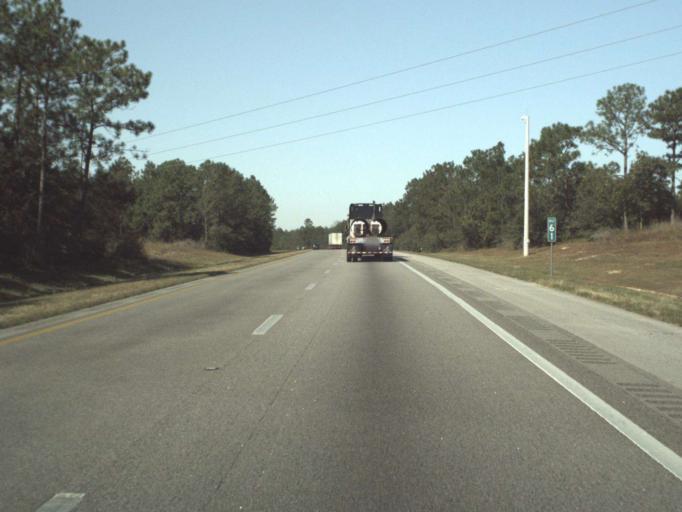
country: US
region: Florida
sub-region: Okaloosa County
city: Crestview
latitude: 30.7260
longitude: -86.4894
